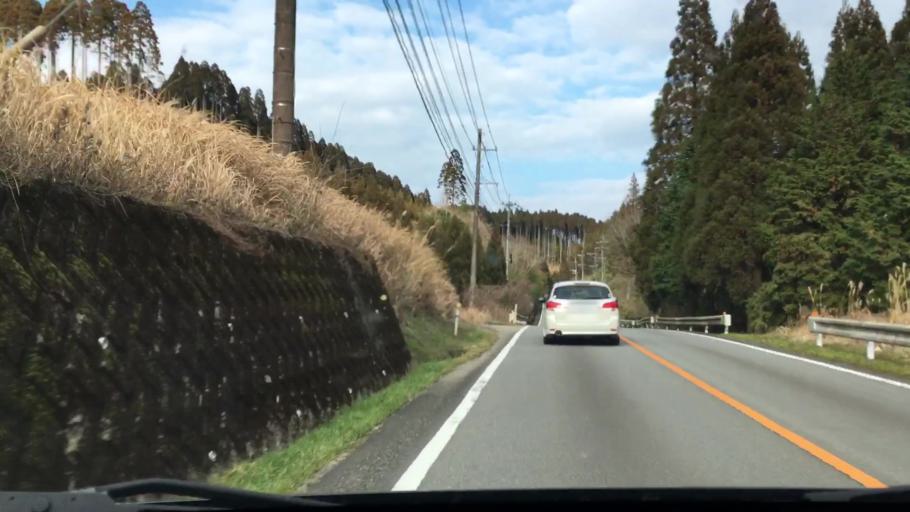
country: JP
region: Miyazaki
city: Nichinan
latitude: 31.7197
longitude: 131.3253
